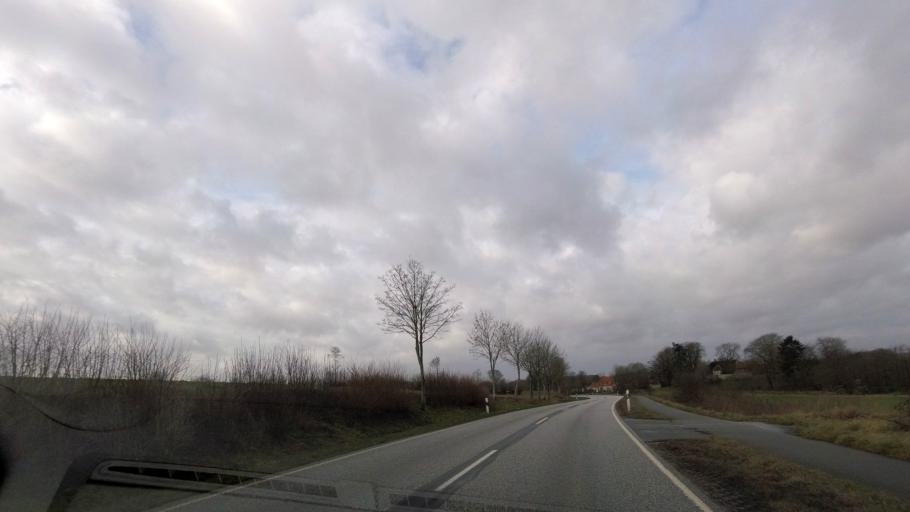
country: DE
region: Schleswig-Holstein
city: Rabenkirchen-Fauluck
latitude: 54.6451
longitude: 9.8539
